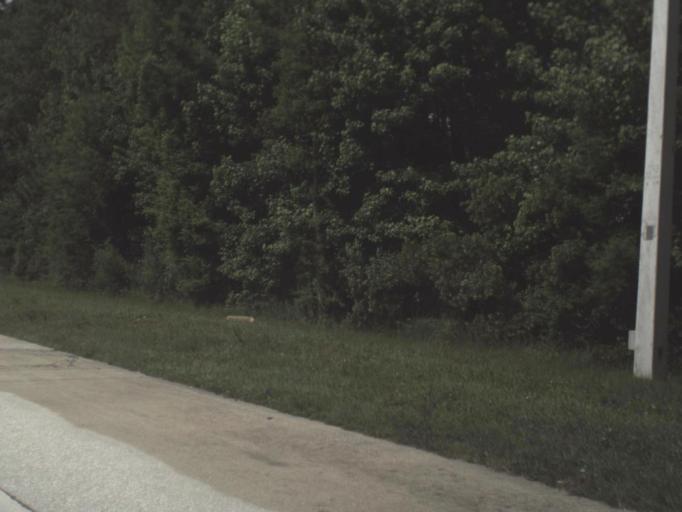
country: US
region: Florida
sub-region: Saint Johns County
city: Fruit Cove
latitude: 30.2143
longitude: -81.5667
